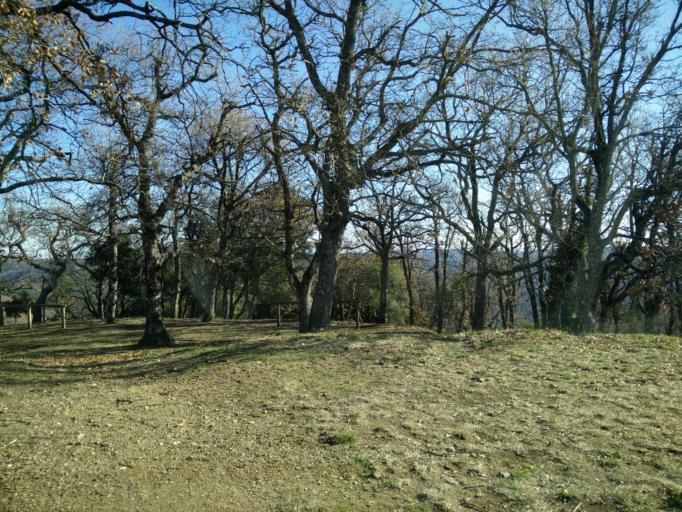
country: FR
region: Provence-Alpes-Cote d'Azur
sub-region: Departement du Var
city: Gonfaron
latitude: 43.2816
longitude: 6.2947
